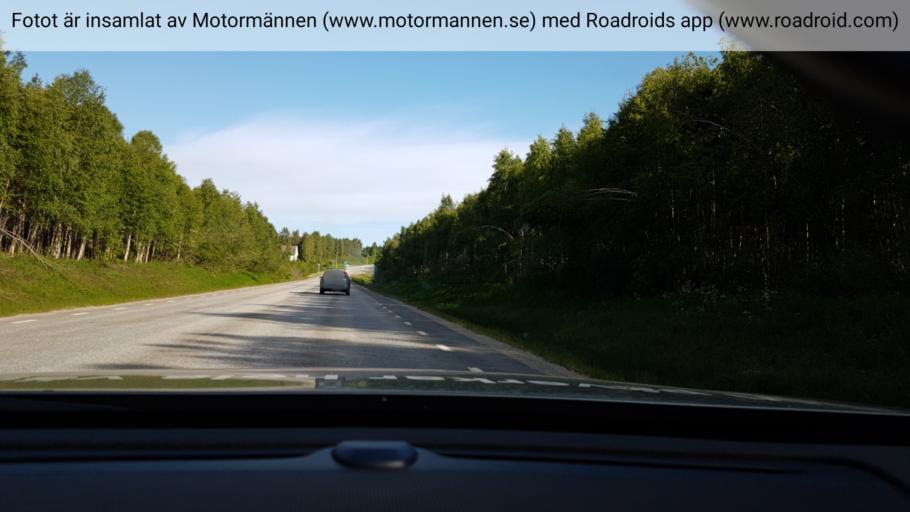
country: SE
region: Vaesterbotten
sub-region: Vannas Kommun
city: Vaennaes
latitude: 63.9946
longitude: 19.7296
